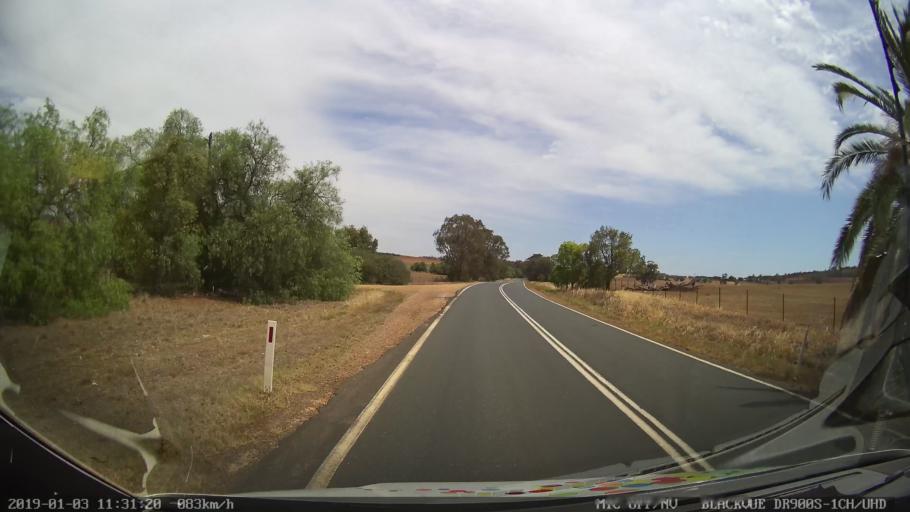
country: AU
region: New South Wales
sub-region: Weddin
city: Grenfell
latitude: -33.9716
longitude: 148.1842
